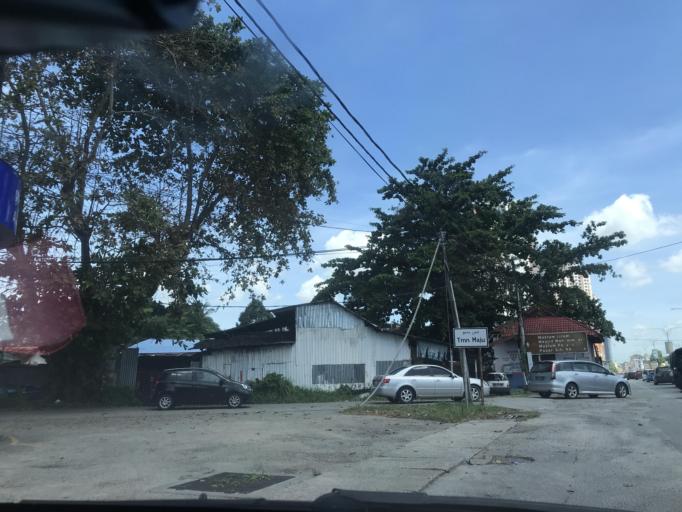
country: MY
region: Kelantan
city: Kota Bharu
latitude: 6.1098
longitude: 102.2544
